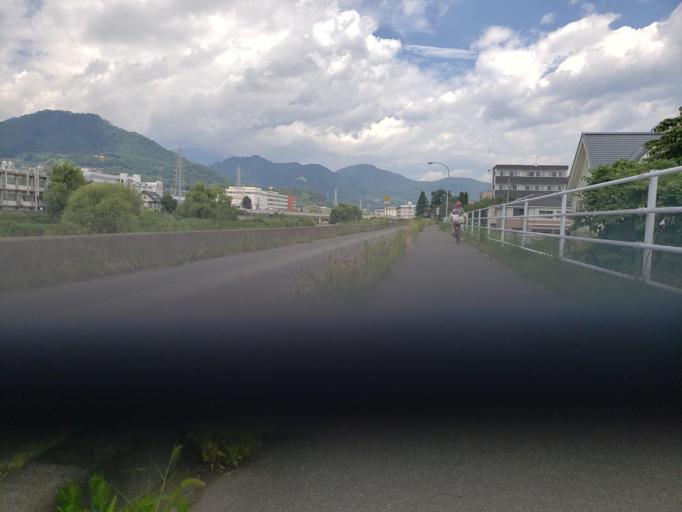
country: JP
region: Nagano
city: Nagano-shi
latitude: 36.6345
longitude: 138.1797
